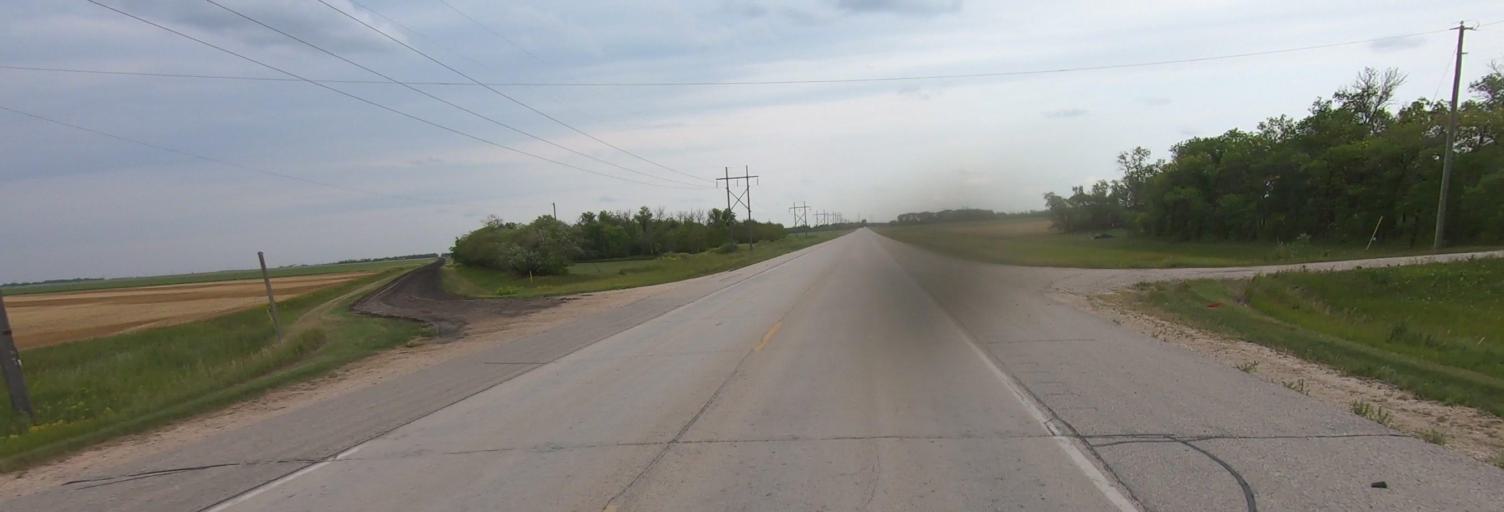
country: CA
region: Manitoba
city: Headingley
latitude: 49.7284
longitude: -97.3681
